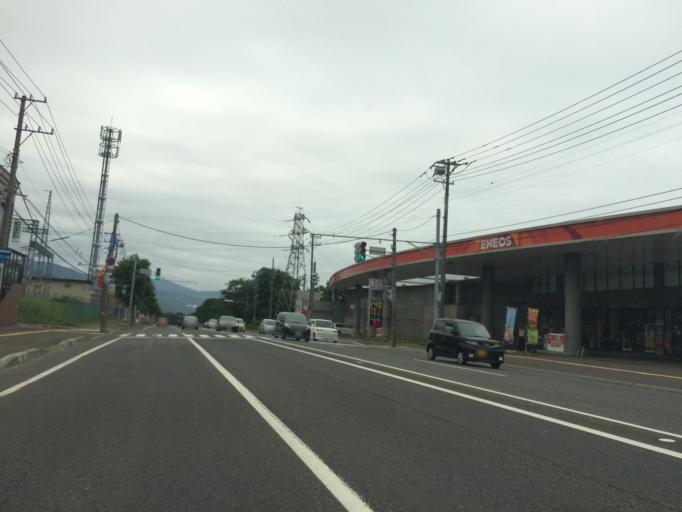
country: JP
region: Hokkaido
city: Sapporo
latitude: 43.1310
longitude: 141.2059
